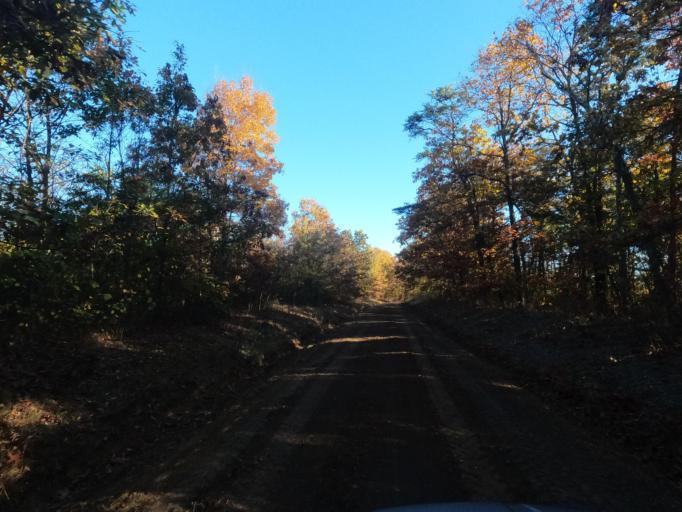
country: US
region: West Virginia
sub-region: Mineral County
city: Fort Ashby
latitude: 39.5554
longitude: -78.5271
